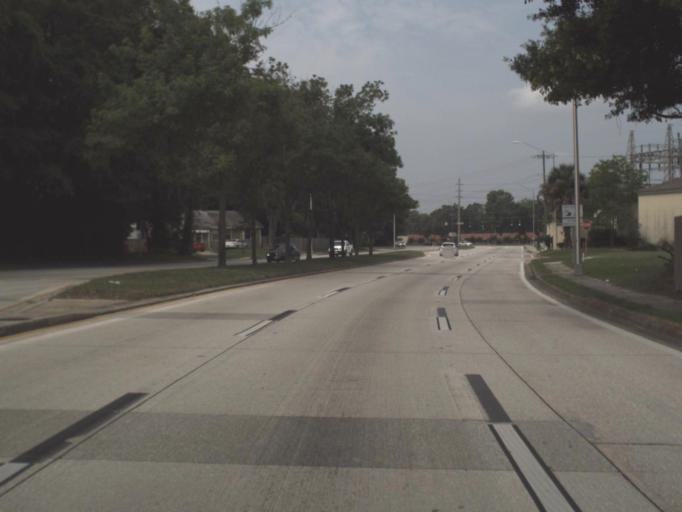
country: US
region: Florida
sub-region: Duval County
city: Jacksonville
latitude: 30.3105
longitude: -81.7063
